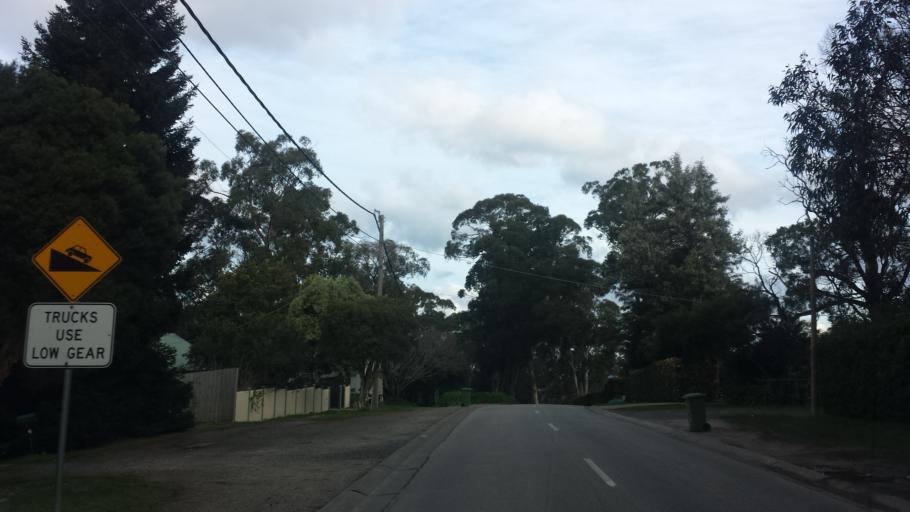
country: AU
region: Victoria
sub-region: Yarra Ranges
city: Belgrave
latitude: -37.9034
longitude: 145.3521
